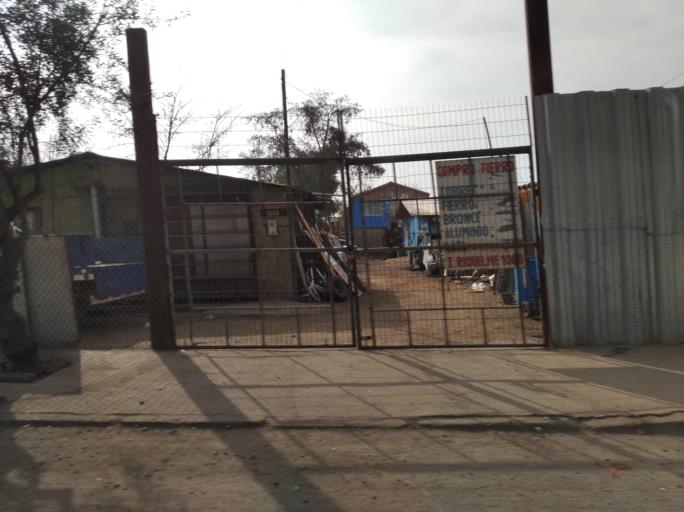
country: CL
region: Santiago Metropolitan
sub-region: Provincia de Chacabuco
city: Lampa
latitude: -33.2899
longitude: -70.8864
